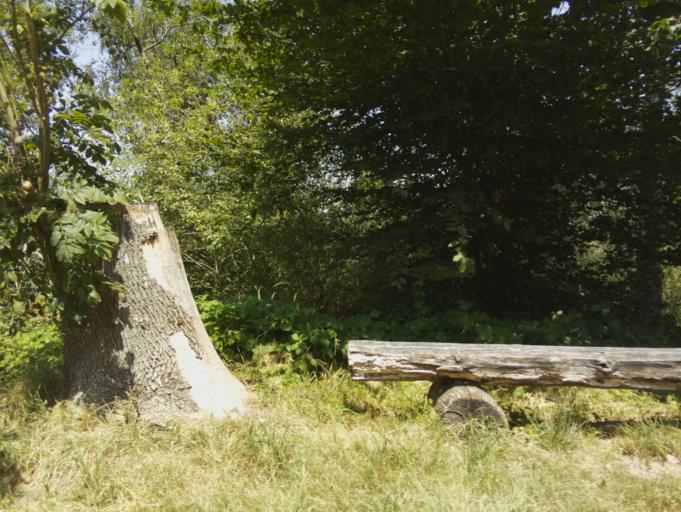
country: CH
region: Zurich
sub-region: Bezirk Andelfingen
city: Kleinandelfingen
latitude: 47.6204
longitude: 8.7048
